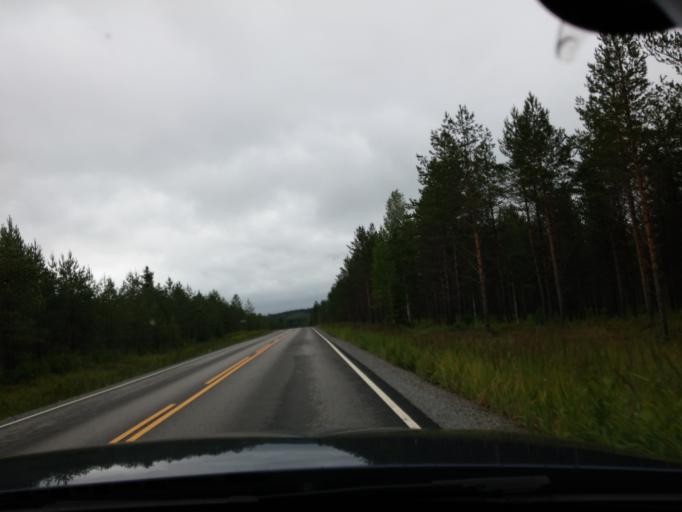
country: FI
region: Central Finland
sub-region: Saarijaervi-Viitasaari
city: Pylkoenmaeki
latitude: 62.6403
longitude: 24.8584
